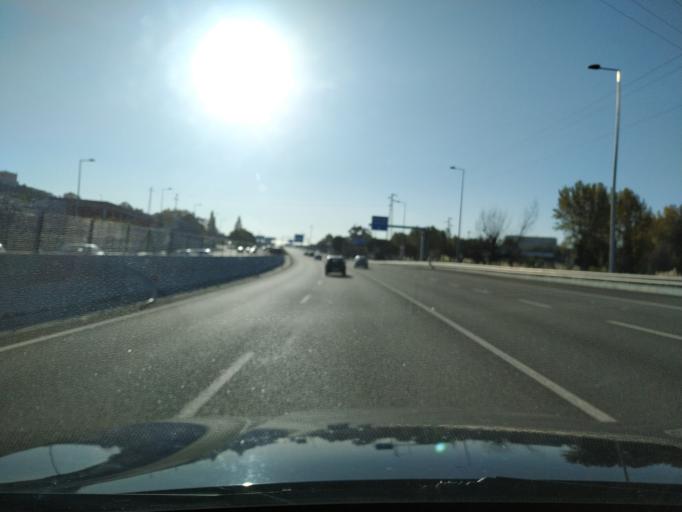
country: PT
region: Porto
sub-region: Vila Nova de Gaia
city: Vilar de Andorinho
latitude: 41.1033
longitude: -8.6017
